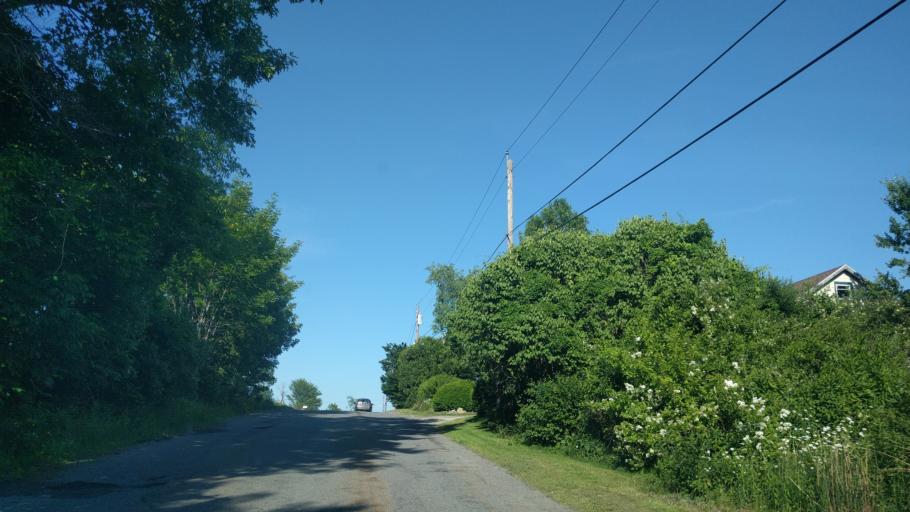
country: US
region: Massachusetts
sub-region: Worcester County
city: Oxford
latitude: 42.1430
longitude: -71.8419
